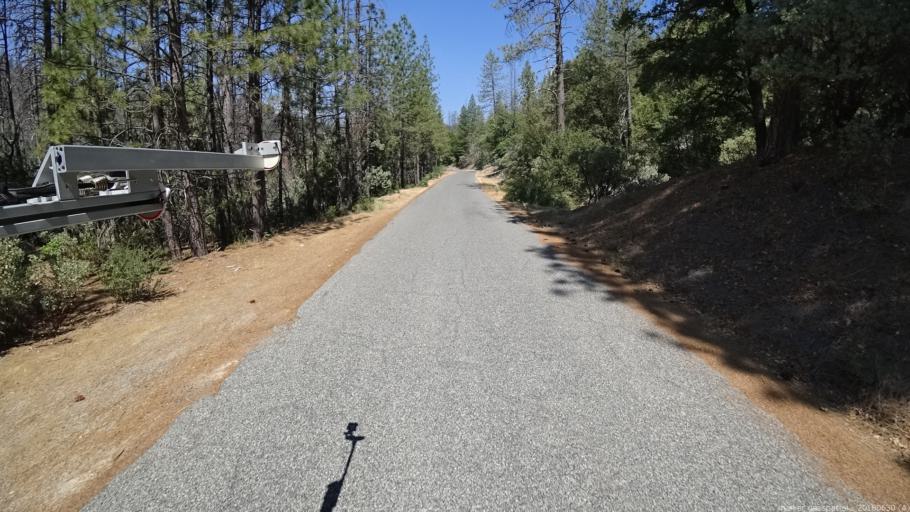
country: US
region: California
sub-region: Madera County
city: Oakhurst
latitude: 37.3601
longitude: -119.3477
